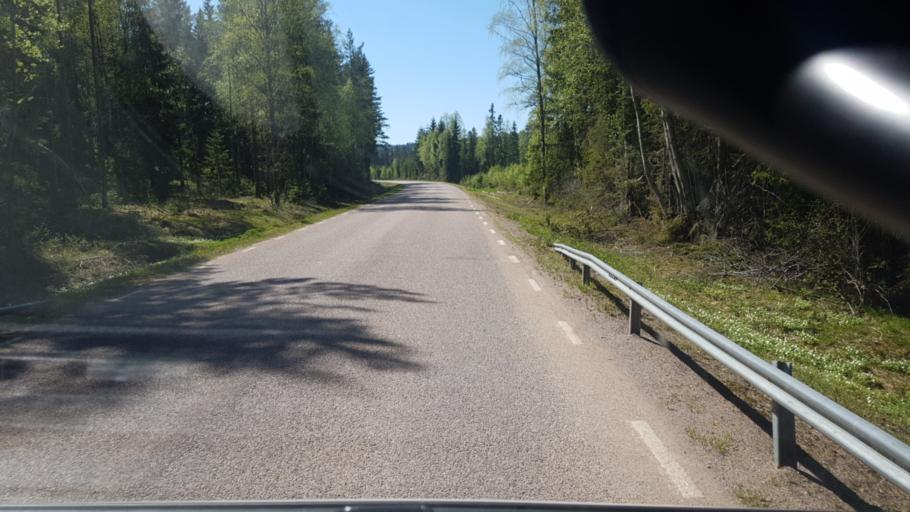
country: SE
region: Vaermland
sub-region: Sunne Kommun
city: Sunne
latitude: 59.8226
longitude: 12.8427
